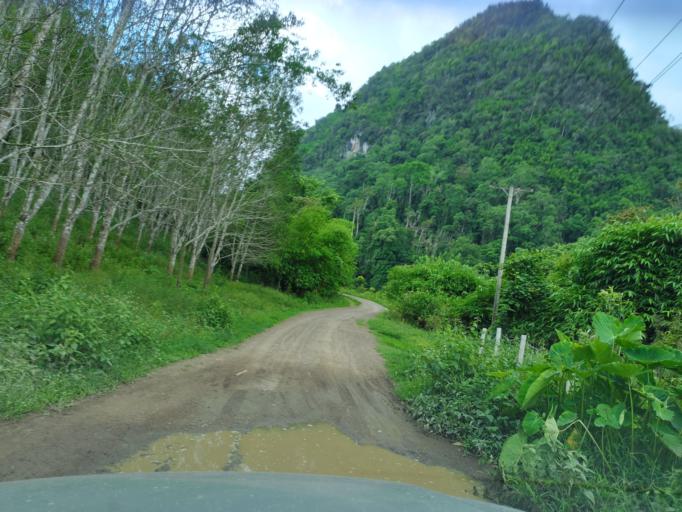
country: LA
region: Loungnamtha
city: Muang Long
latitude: 20.7810
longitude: 101.0165
